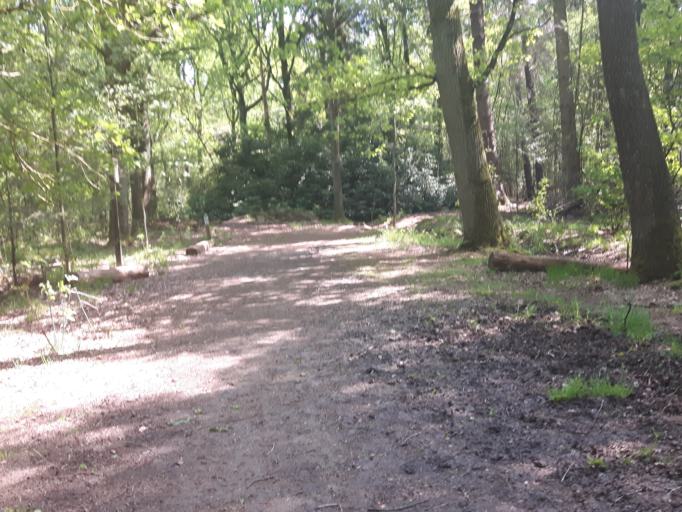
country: NL
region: Overijssel
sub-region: Gemeente Enschede
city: Enschede
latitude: 52.1451
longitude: 6.8722
